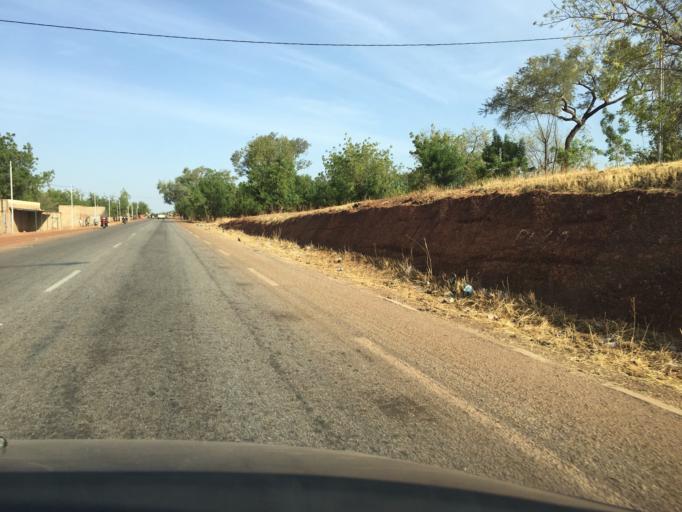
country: BF
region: Plateau-Central
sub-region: Province du Kourweogo
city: Bousse
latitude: 12.5263
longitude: -1.7706
